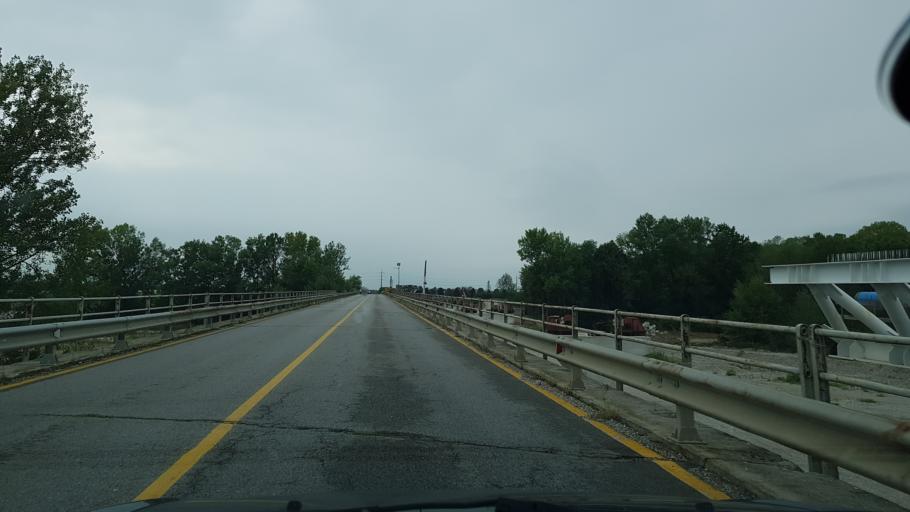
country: IT
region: Friuli Venezia Giulia
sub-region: Provincia di Udine
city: Chiopris
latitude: 45.9250
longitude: 13.3786
